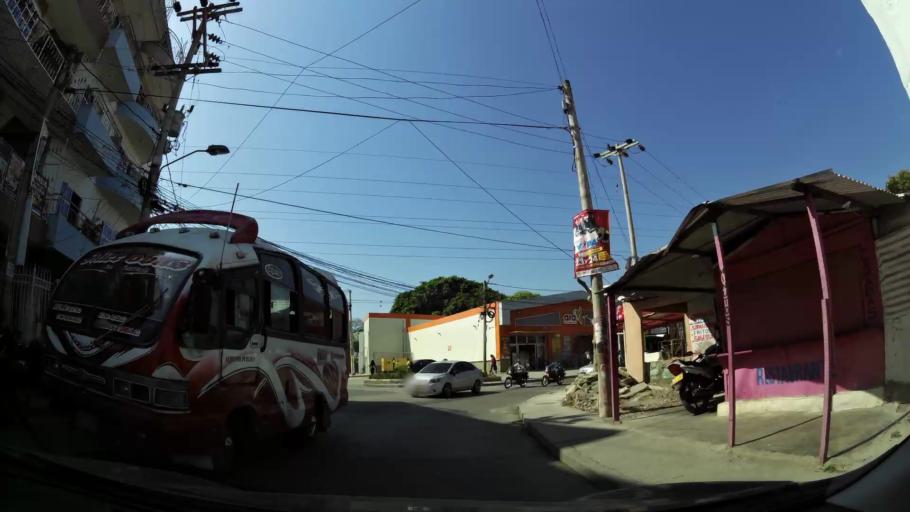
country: CO
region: Bolivar
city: Cartagena
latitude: 10.3789
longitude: -75.4715
